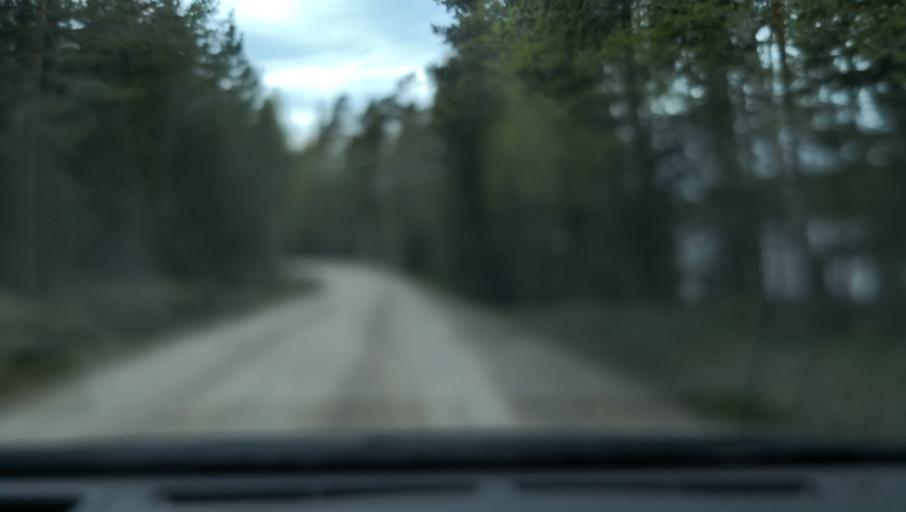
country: SE
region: Vaestmanland
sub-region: Norbergs Kommun
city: Norberg
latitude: 60.0914
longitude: 15.8582
